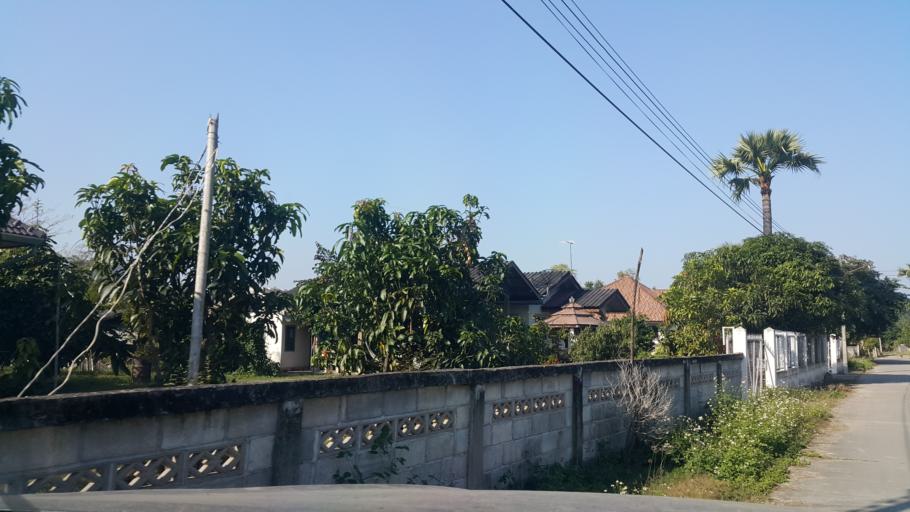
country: TH
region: Chiang Mai
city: Mae On
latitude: 18.7276
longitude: 99.2006
